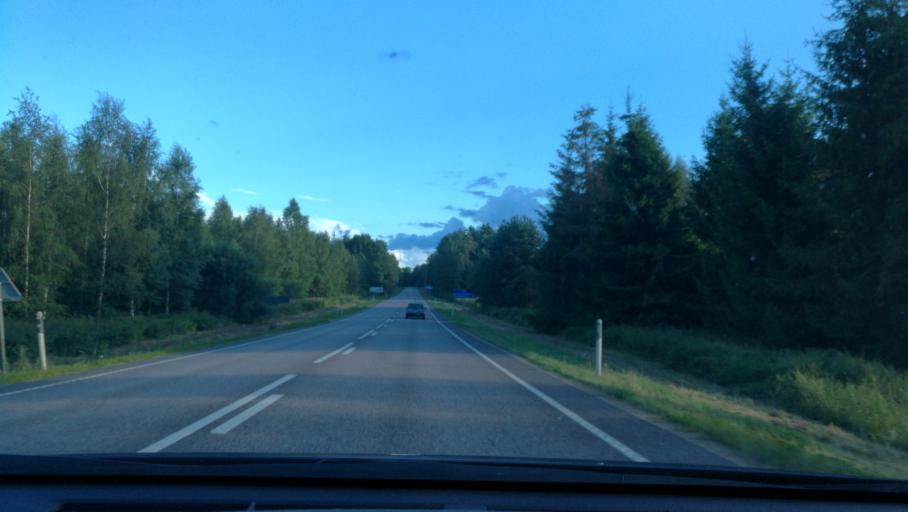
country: SE
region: Vaestmanland
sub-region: Kungsors Kommun
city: Kungsoer
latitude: 59.2760
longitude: 16.1194
